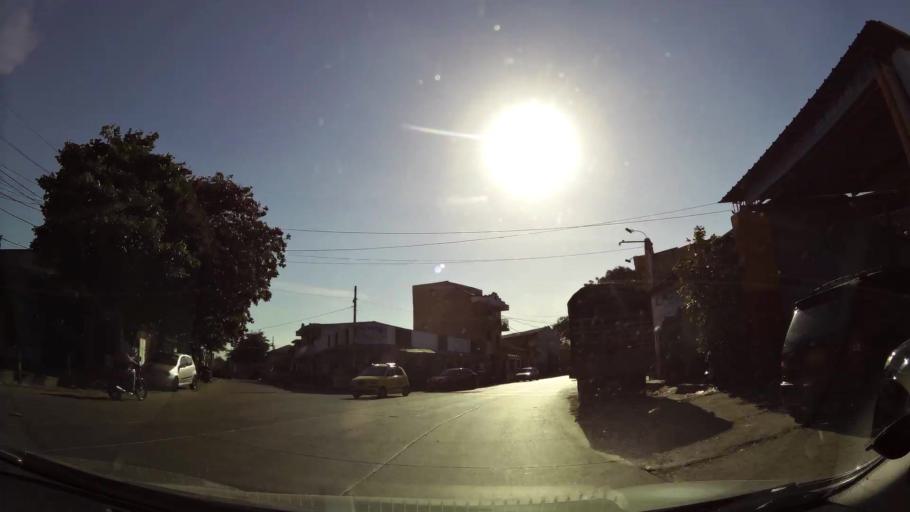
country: CO
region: Atlantico
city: Barranquilla
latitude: 10.9677
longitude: -74.7865
